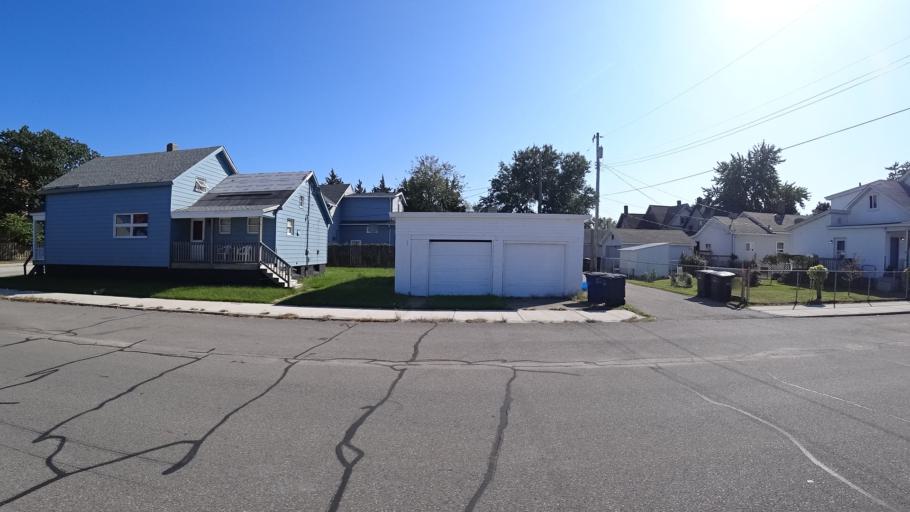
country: US
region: Indiana
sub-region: LaPorte County
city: Michigan City
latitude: 41.7106
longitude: -86.9048
